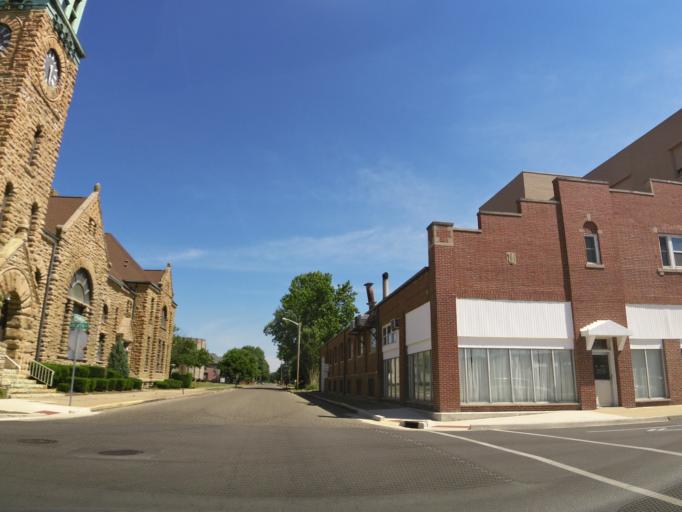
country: US
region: Illinois
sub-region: Vermilion County
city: Danville
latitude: 40.1262
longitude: -87.6326
